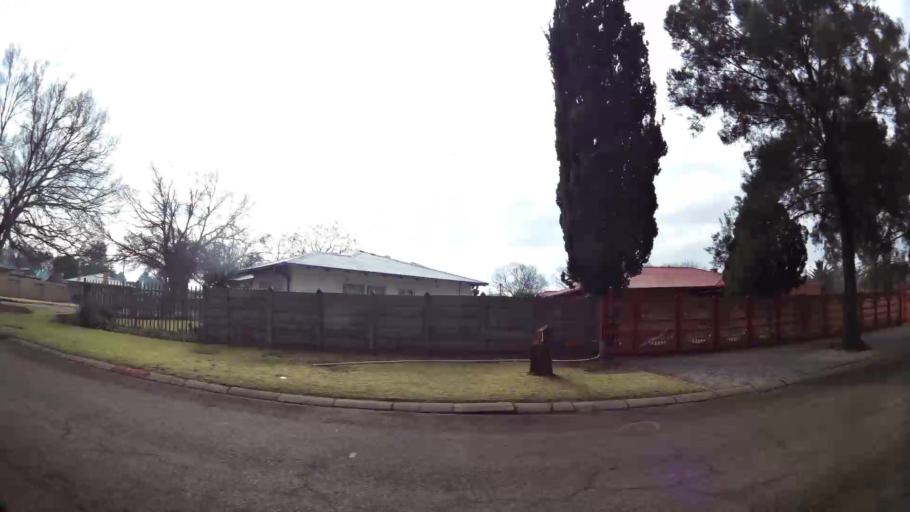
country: ZA
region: Gauteng
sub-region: Sedibeng District Municipality
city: Vanderbijlpark
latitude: -26.7029
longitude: 27.8278
